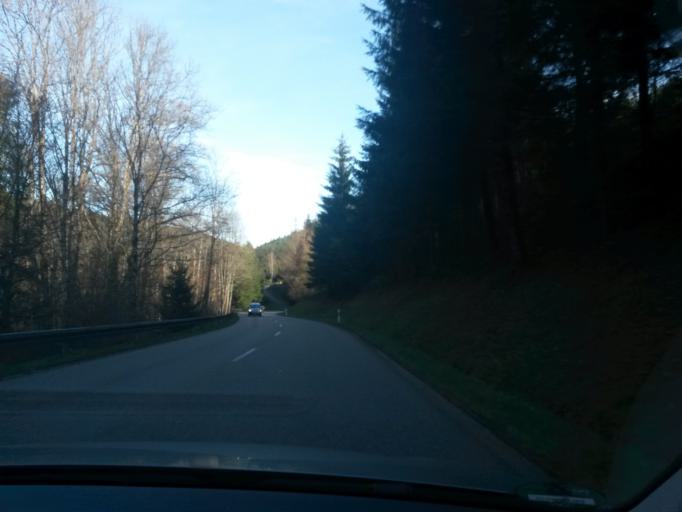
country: DE
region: Baden-Wuerttemberg
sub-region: Freiburg Region
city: Muhlenbach
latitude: 48.2262
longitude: 8.1001
